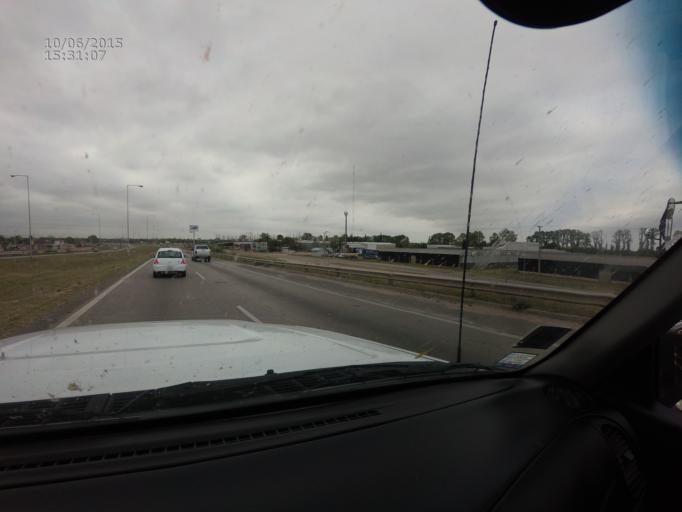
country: AR
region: Cordoba
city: Malvinas Argentinas
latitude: -31.3750
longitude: -64.1274
